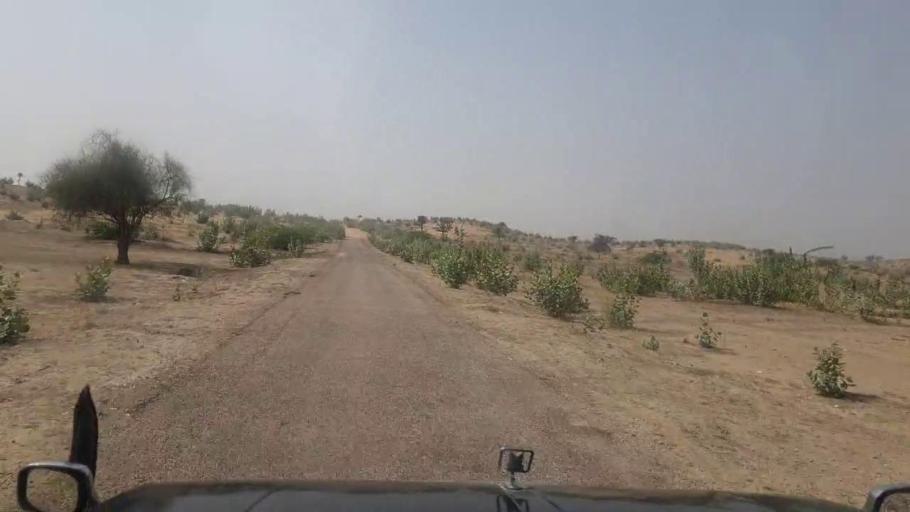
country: PK
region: Sindh
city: Islamkot
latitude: 25.0757
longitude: 70.1508
